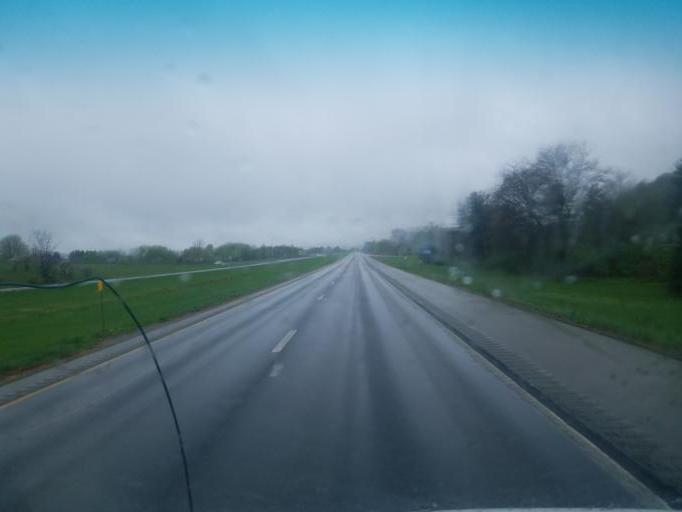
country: US
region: New York
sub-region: Cattaraugus County
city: Allegany
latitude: 42.1029
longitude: -78.5082
